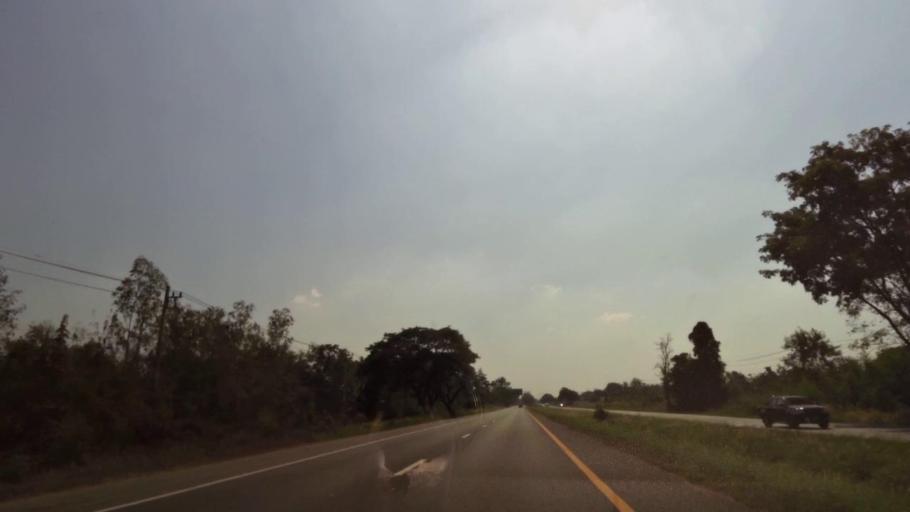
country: TH
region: Phichit
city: Bueng Na Rang
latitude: 16.1980
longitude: 100.1282
